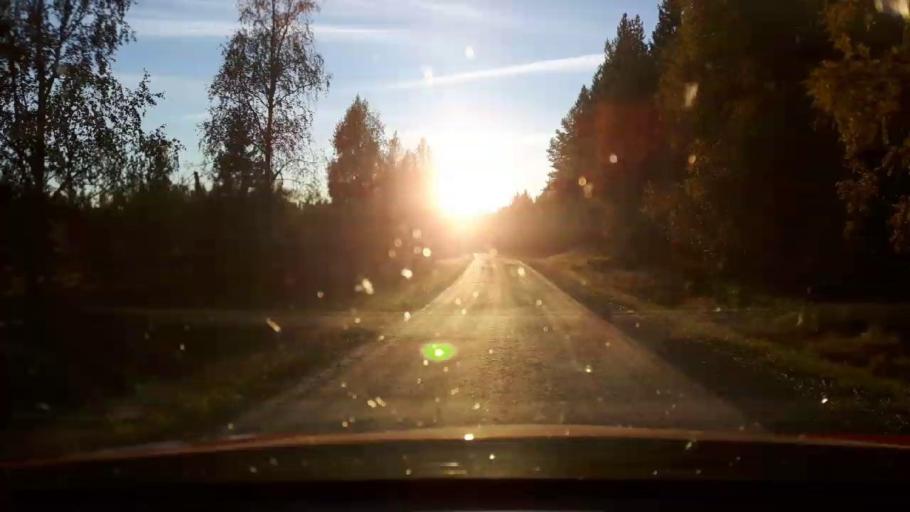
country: SE
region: Jaemtland
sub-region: Krokoms Kommun
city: Krokom
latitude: 63.4635
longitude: 14.3767
